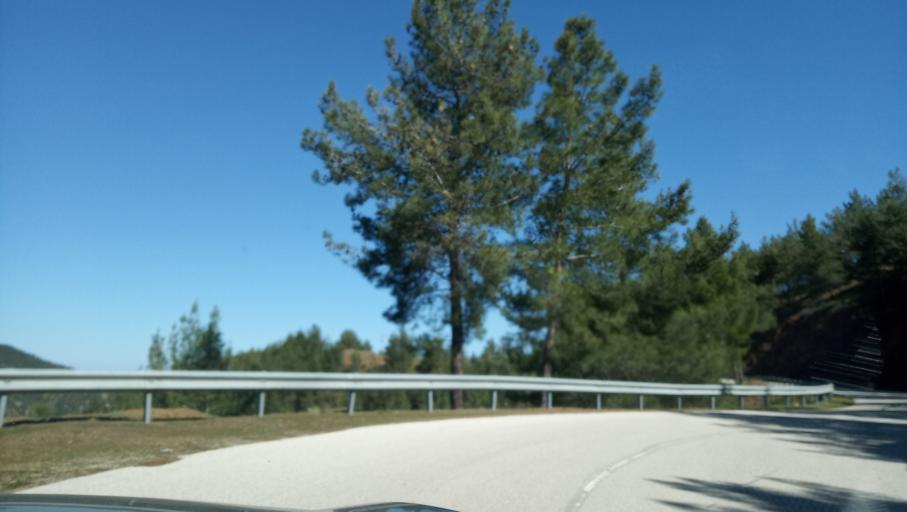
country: CY
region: Lefkosia
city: Lefka
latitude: 35.0717
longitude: 32.7518
